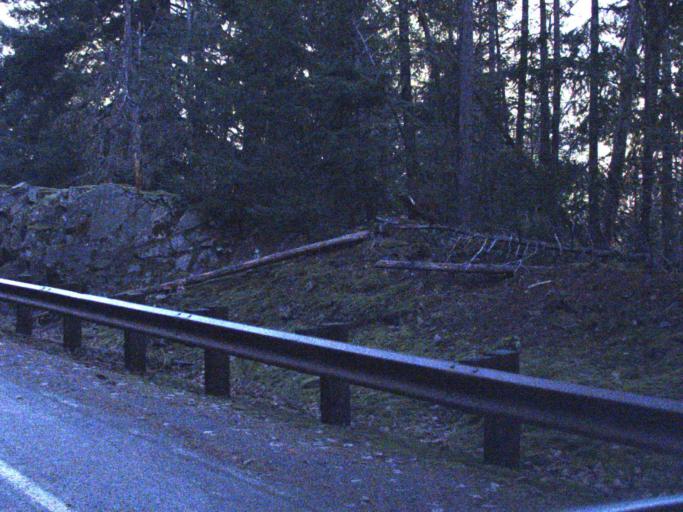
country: US
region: Washington
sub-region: Snohomish County
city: Darrington
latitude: 48.7080
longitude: -121.1165
